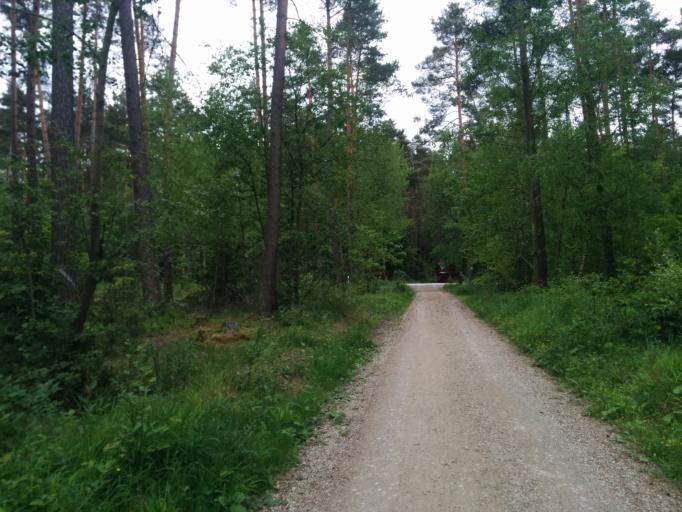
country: DE
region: Bavaria
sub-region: Regierungsbezirk Mittelfranken
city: Kalchreuth
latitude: 49.5351
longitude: 11.0817
